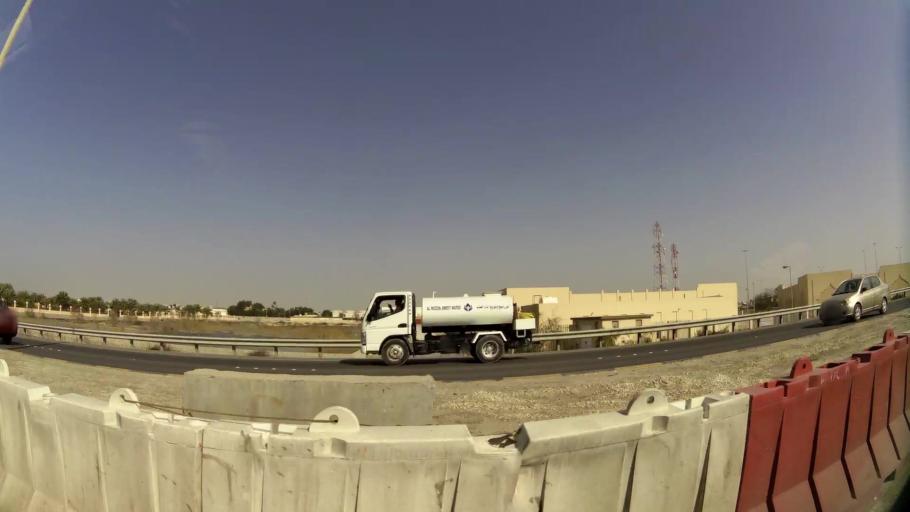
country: BH
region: Central Governorate
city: Madinat Hamad
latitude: 26.1756
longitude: 50.4655
